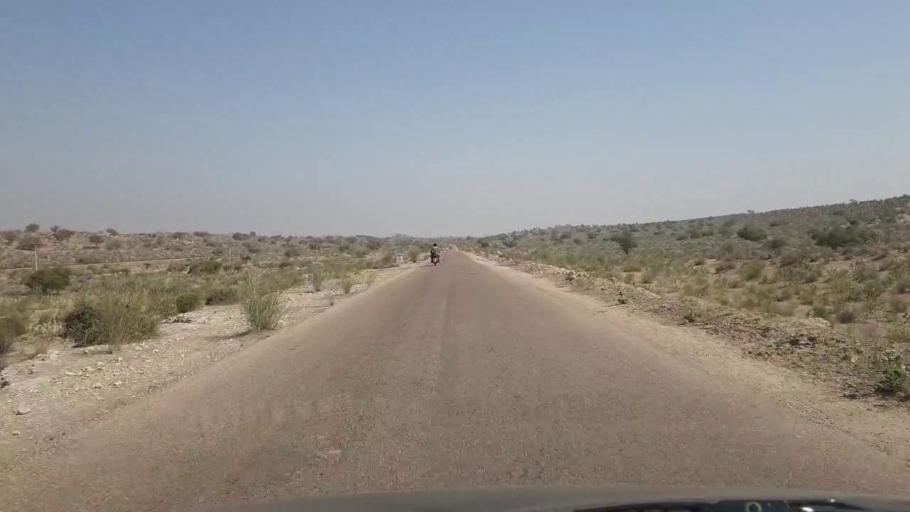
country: PK
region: Sindh
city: Chor
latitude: 25.6158
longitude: 70.0508
